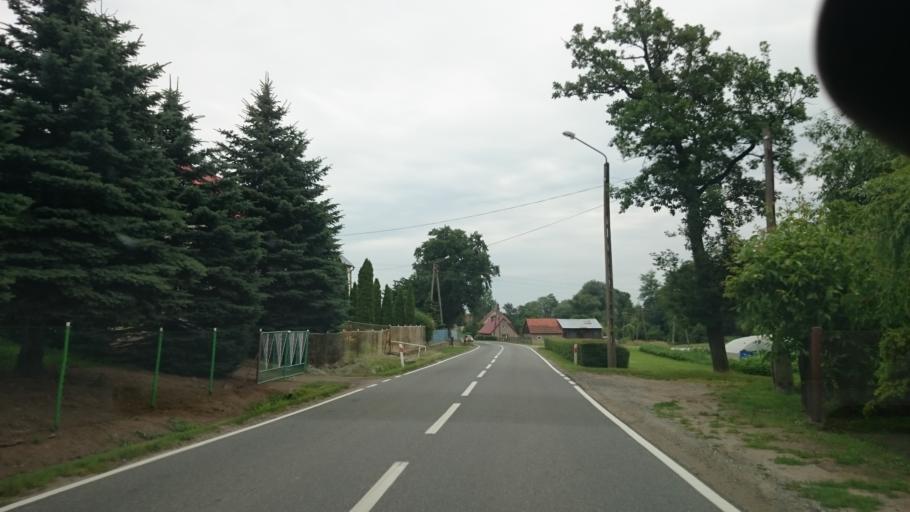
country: PL
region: Lower Silesian Voivodeship
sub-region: Powiat zabkowicki
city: Kamieniec Zabkowicki
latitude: 50.5820
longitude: 16.9329
